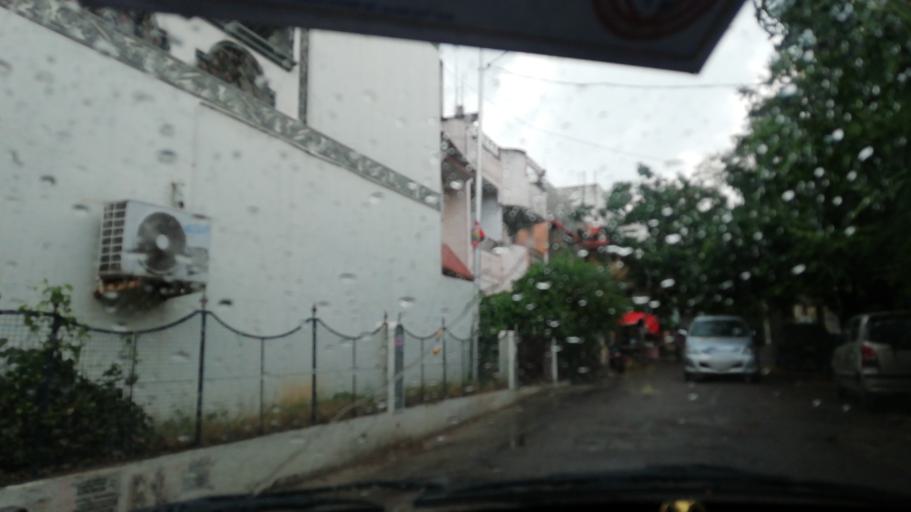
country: IN
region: Telangana
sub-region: Hyderabad
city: Hyderabad
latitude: 17.3932
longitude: 78.4351
